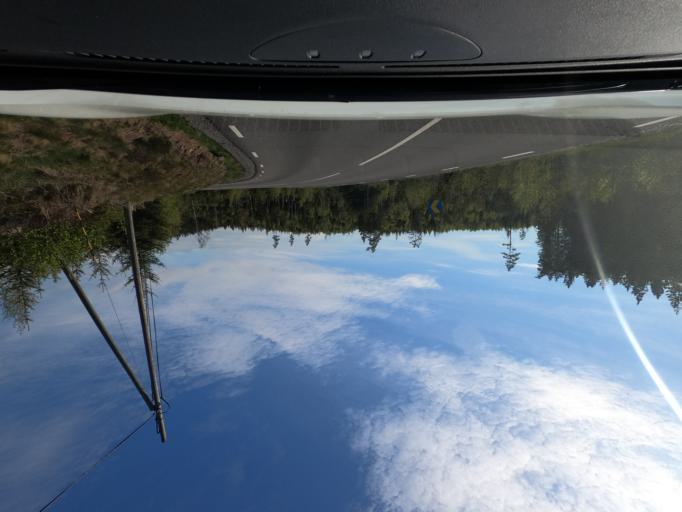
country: SE
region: Vaestra Goetaland
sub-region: Harryda Kommun
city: Landvetter
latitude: 57.6315
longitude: 12.2660
